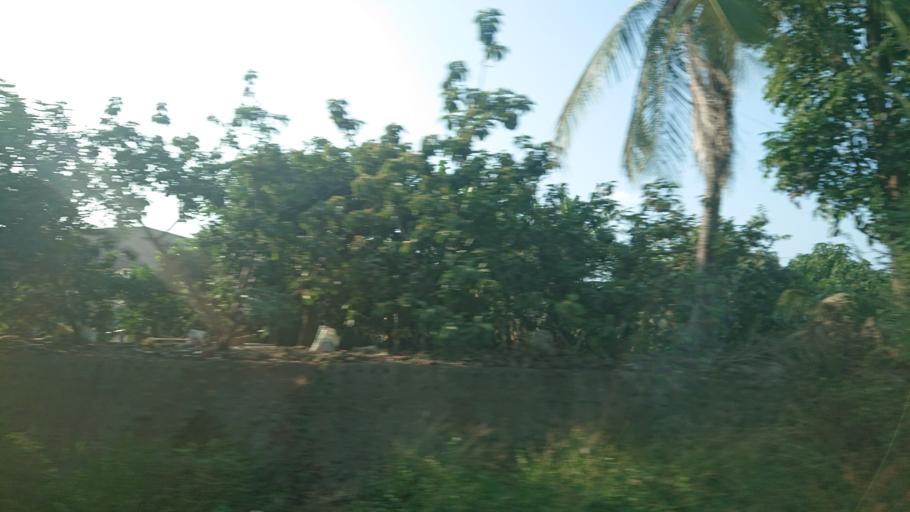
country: TW
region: Taiwan
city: Xinying
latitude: 23.1672
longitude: 120.2534
